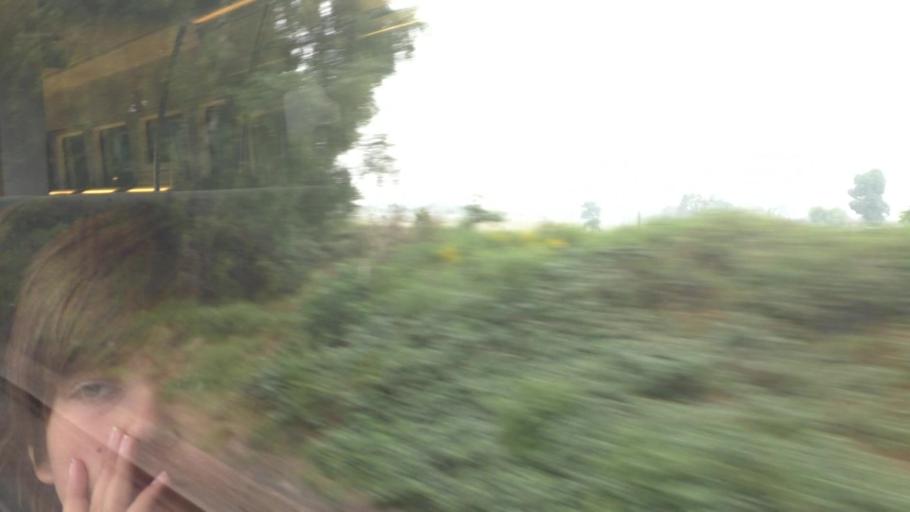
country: DE
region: Saxony
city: Grossrohrsdorf
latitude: 51.0971
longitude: 14.0418
